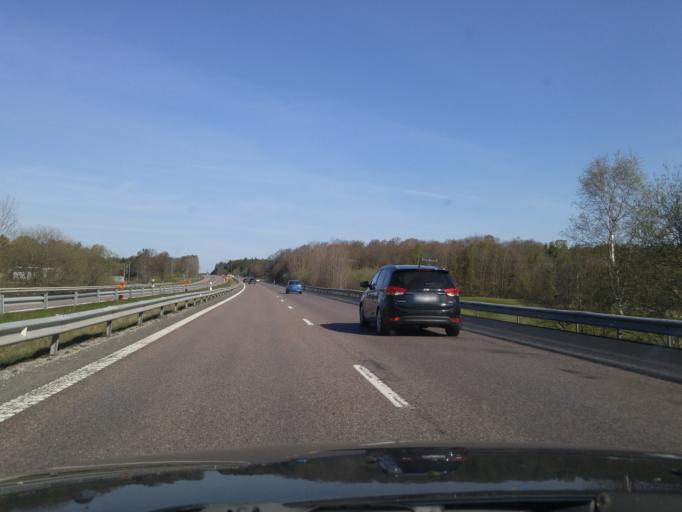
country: SE
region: Vaestra Goetaland
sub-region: Kungalvs Kommun
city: Kode
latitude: 57.9340
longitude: 11.8706
